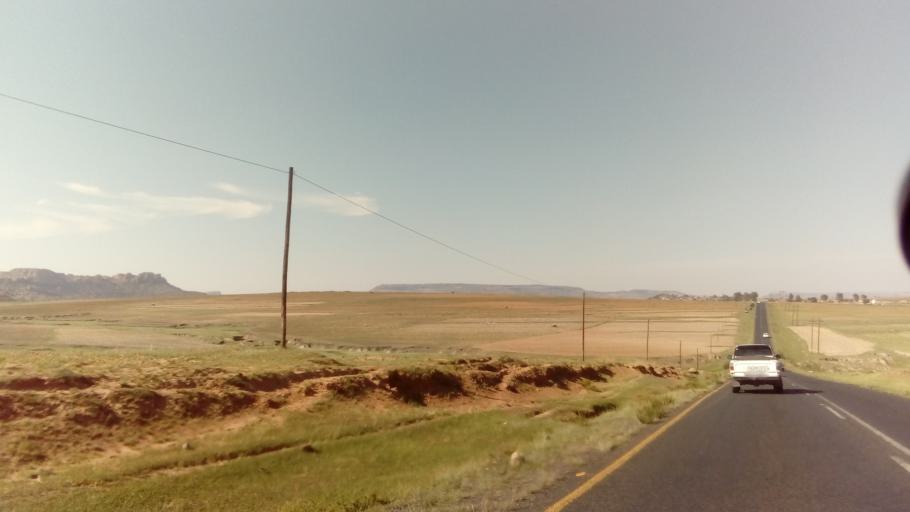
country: LS
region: Berea
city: Teyateyaneng
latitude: -29.1730
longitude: 27.6346
